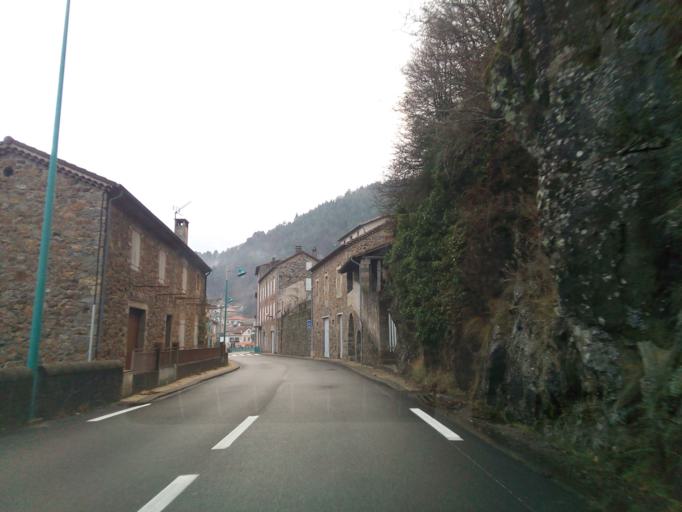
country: FR
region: Rhone-Alpes
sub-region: Departement de l'Ardeche
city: Saint-Sauveur-de-Montagut
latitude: 44.8238
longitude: 4.5787
